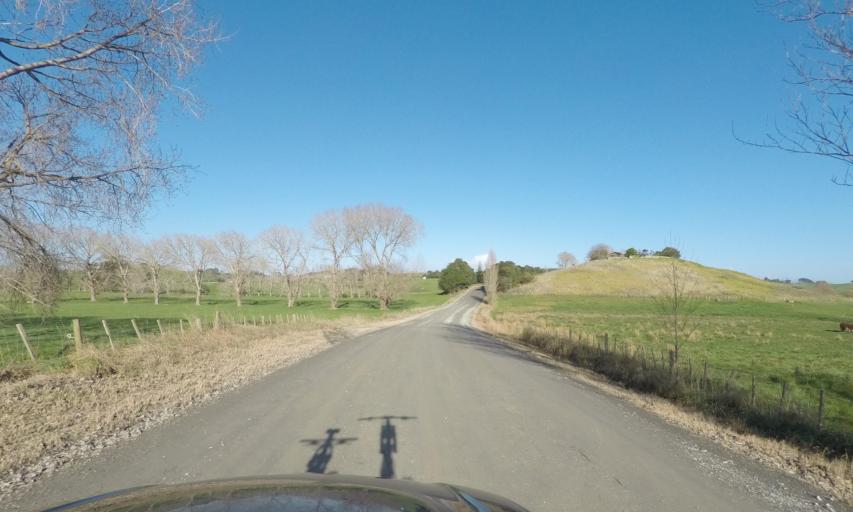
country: NZ
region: Auckland
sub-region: Auckland
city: Wellsford
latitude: -36.1510
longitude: 174.6062
